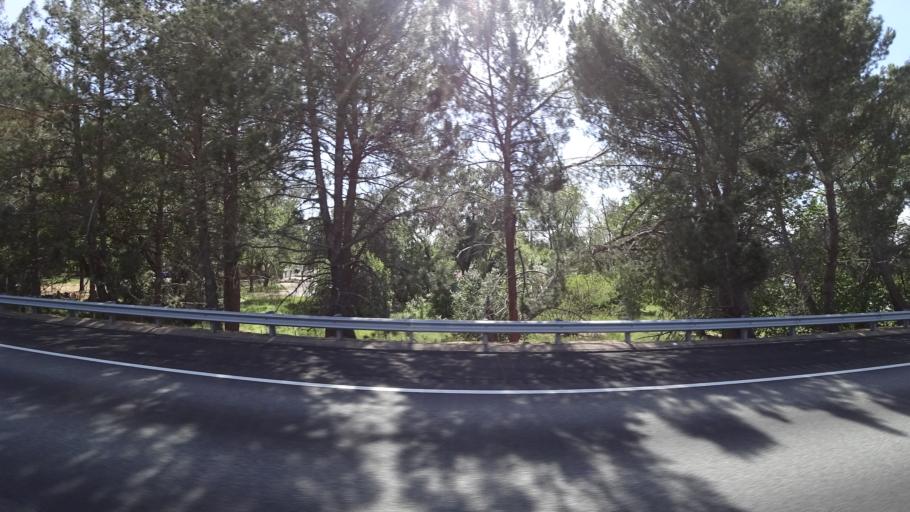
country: US
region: California
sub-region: Shasta County
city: Anderson
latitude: 40.4549
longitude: -122.2946
